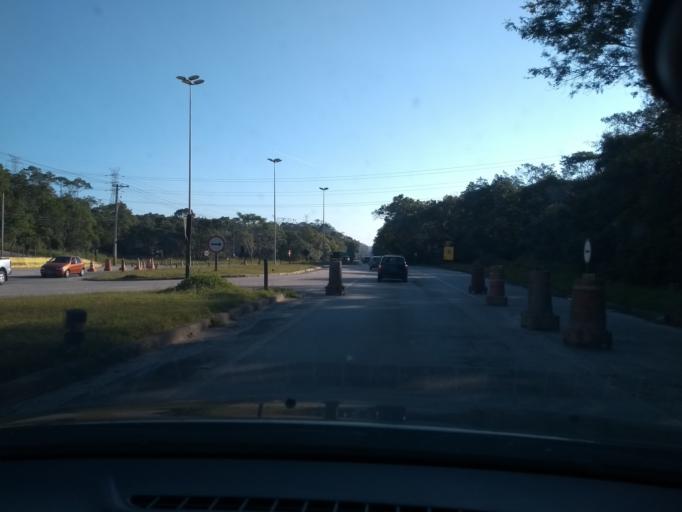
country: BR
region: Sao Paulo
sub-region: Rio Grande Da Serra
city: Rio Grande da Serra
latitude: -23.7669
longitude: -46.4678
